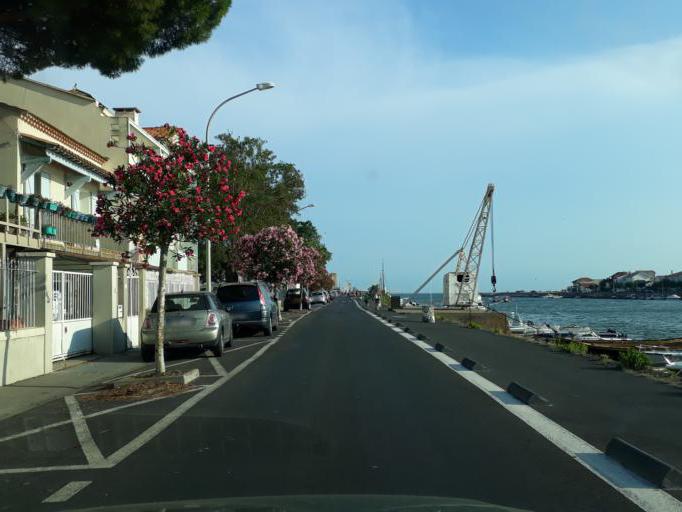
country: FR
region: Languedoc-Roussillon
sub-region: Departement de l'Herault
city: Vias
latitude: 43.2876
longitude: 3.4450
